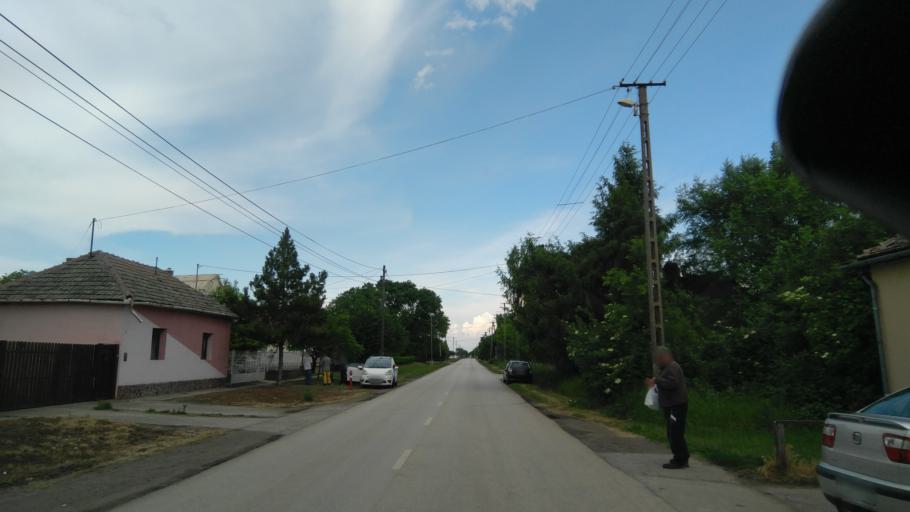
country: HU
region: Bekes
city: Dombegyhaz
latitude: 46.3448
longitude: 21.1462
